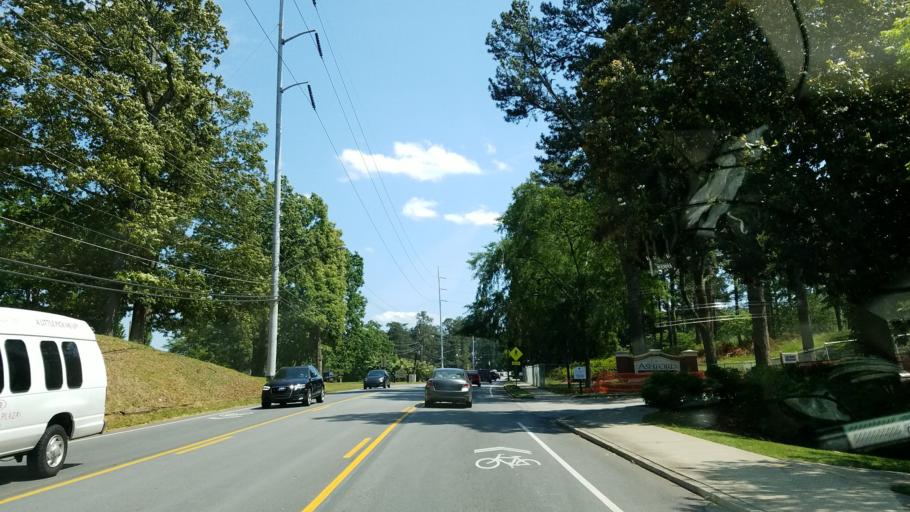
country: US
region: Georgia
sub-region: DeKalb County
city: Chamblee
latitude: 33.8967
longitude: -84.3298
